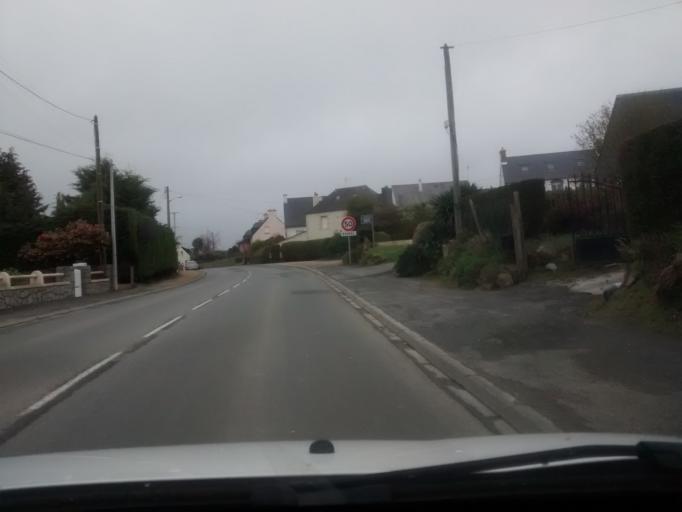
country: FR
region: Brittany
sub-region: Departement des Cotes-d'Armor
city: Trelevern
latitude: 48.8083
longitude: -3.3681
